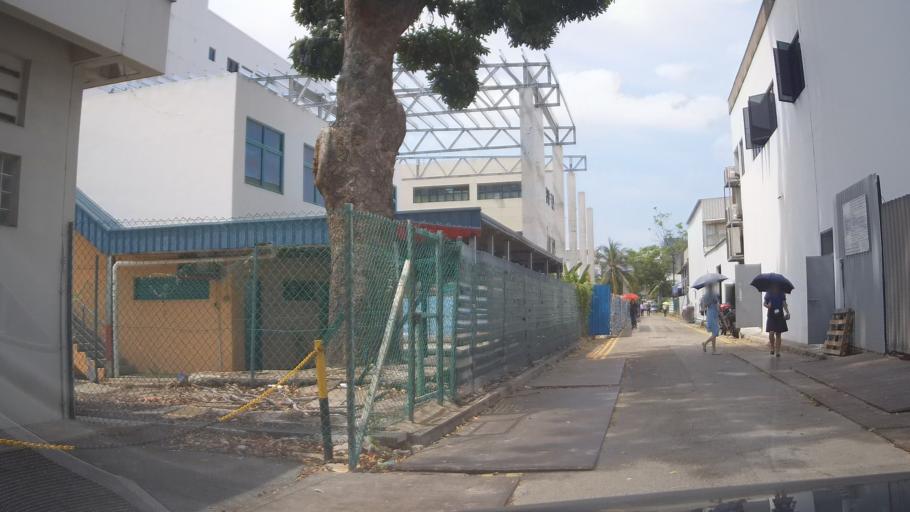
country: SG
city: Singapore
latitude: 1.3345
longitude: 103.9702
